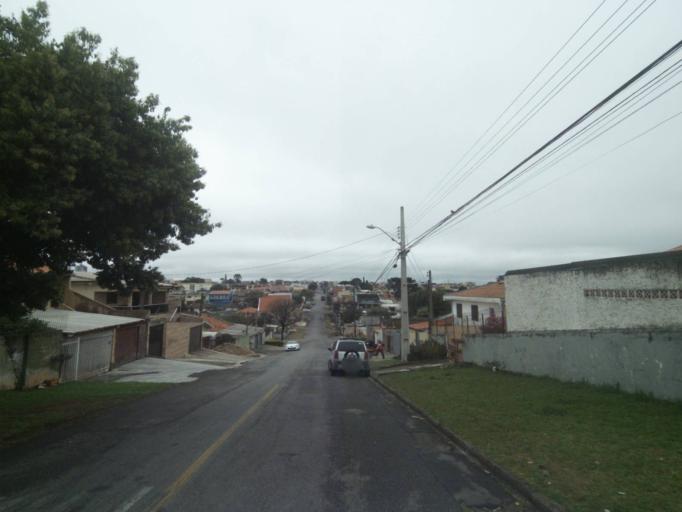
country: BR
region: Parana
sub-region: Curitiba
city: Curitiba
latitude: -25.5052
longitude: -49.3028
